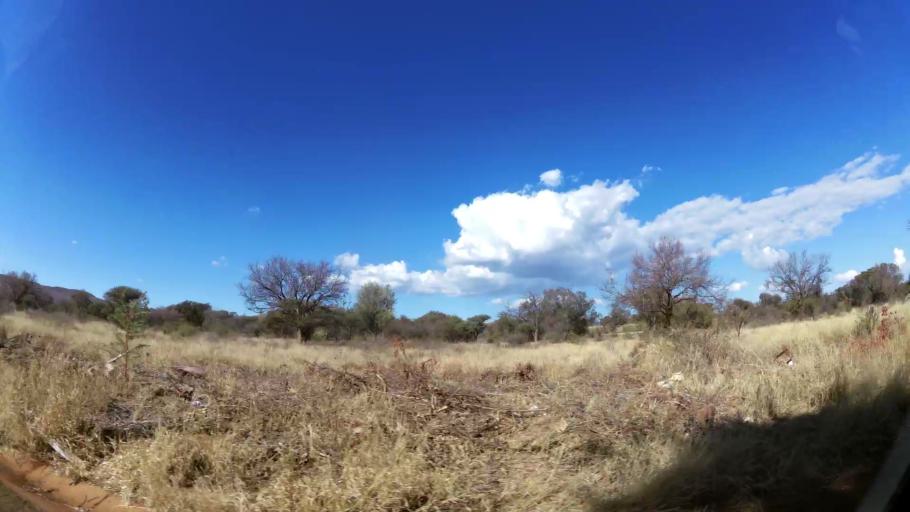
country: ZA
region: Limpopo
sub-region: Waterberg District Municipality
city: Mokopane
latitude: -24.2052
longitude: 29.0117
